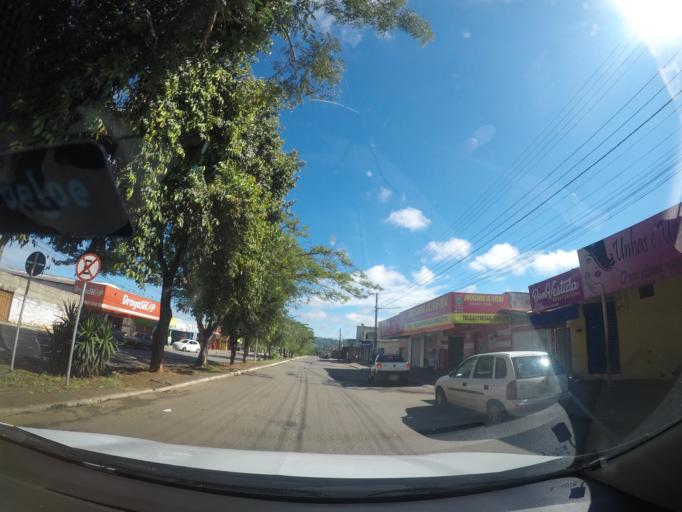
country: BR
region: Goias
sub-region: Senador Canedo
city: Senador Canedo
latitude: -16.6517
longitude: -49.1566
